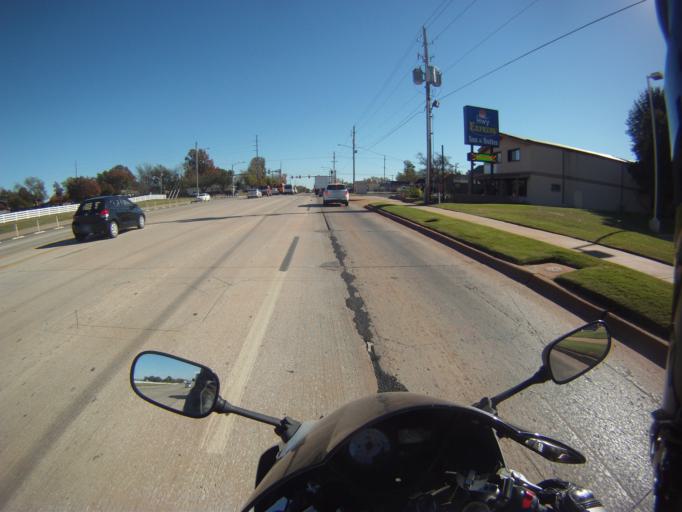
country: US
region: Oklahoma
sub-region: Payne County
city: Stillwater
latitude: 36.1158
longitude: -97.0881
